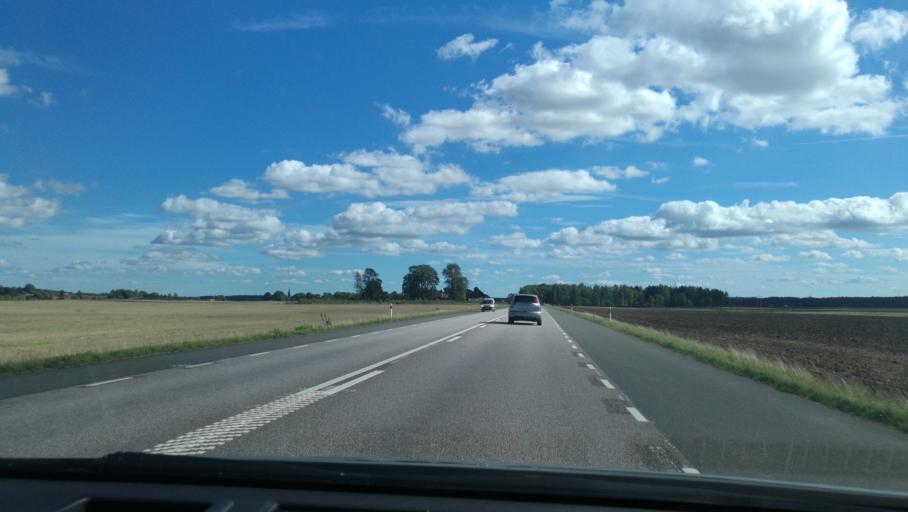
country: SE
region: Vaestra Goetaland
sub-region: Gotene Kommun
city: Kallby
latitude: 58.5096
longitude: 13.3766
